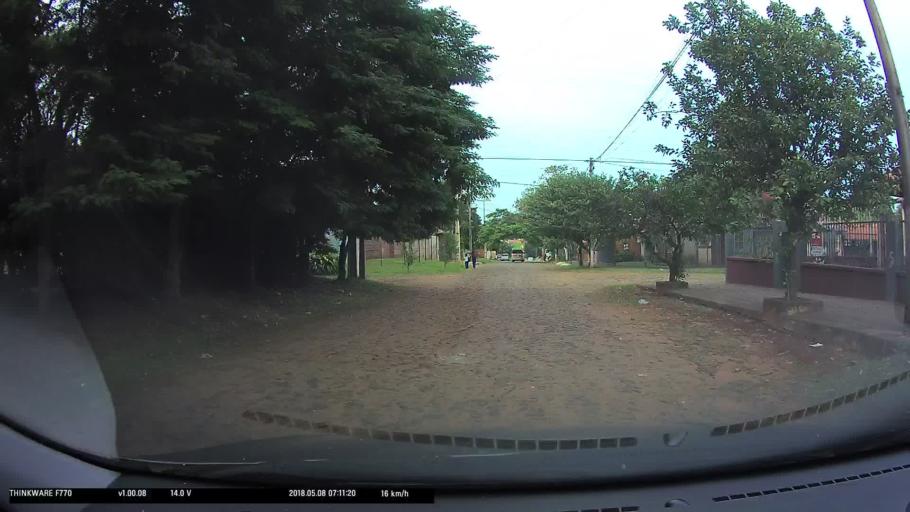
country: PY
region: Central
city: Fernando de la Mora
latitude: -25.2614
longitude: -57.5110
